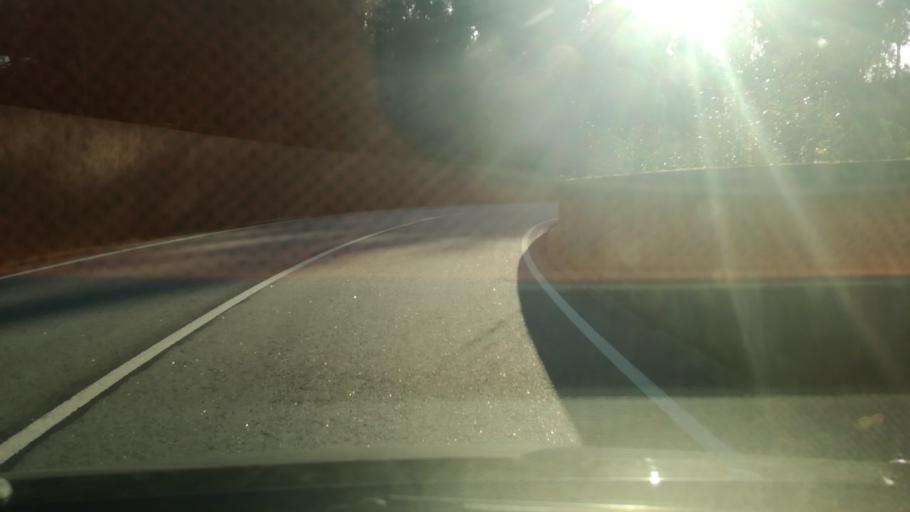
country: PT
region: Porto
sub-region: Trofa
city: Bougado
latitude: 41.3379
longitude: -8.5279
